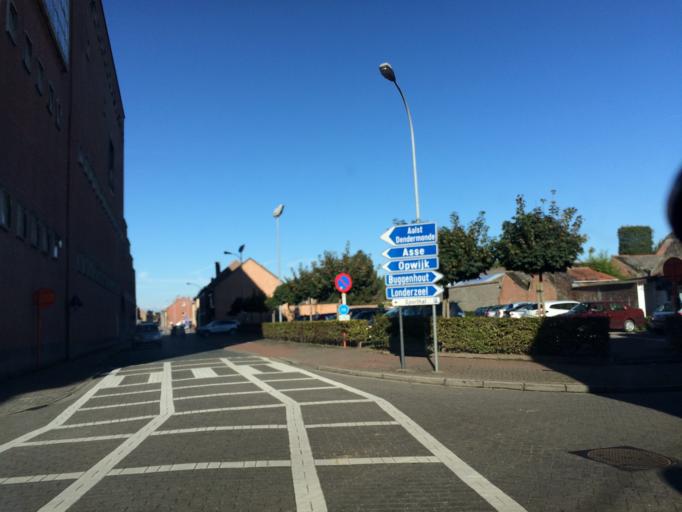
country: BE
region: Flanders
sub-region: Provincie Vlaams-Brabant
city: Merchtem
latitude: 50.9609
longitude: 4.2303
